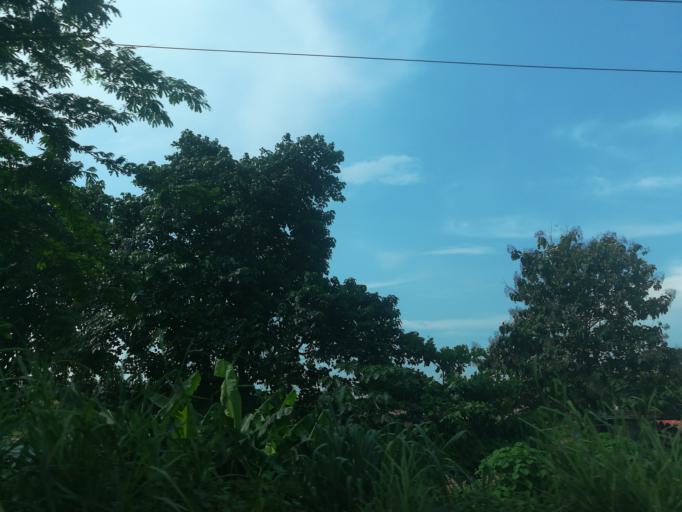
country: NG
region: Lagos
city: Ikorodu
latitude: 6.6312
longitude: 3.5271
